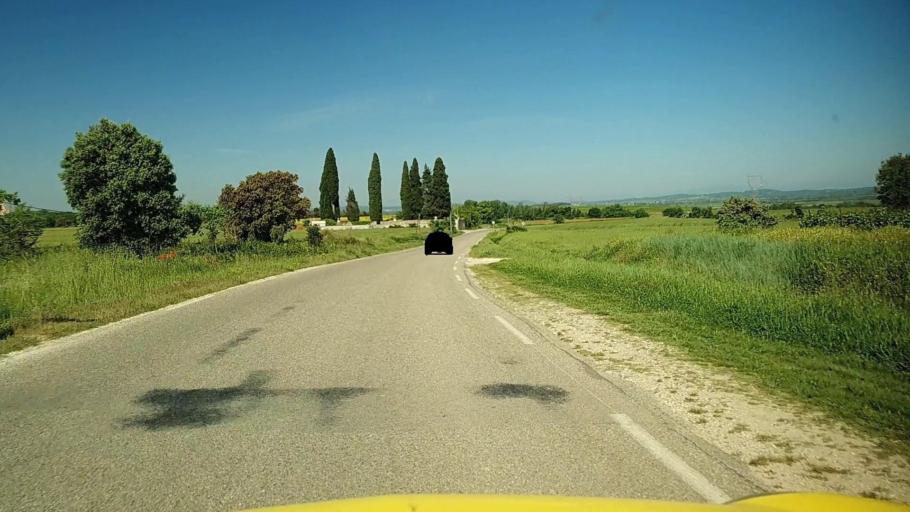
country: FR
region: Languedoc-Roussillon
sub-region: Departement du Gard
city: Blauzac
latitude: 43.9430
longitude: 4.3523
